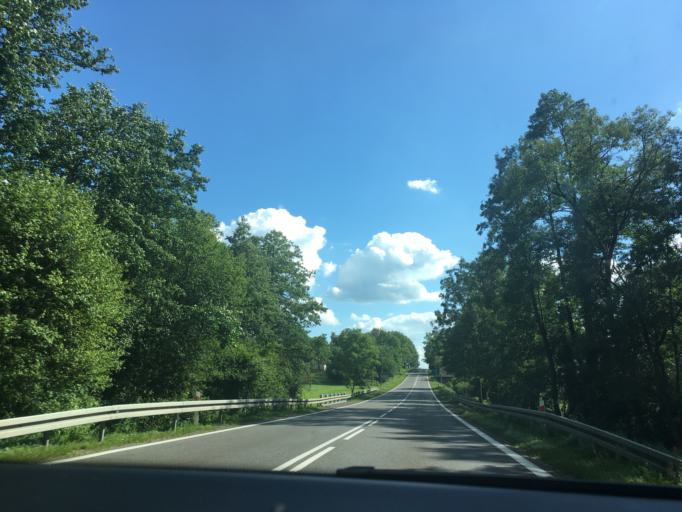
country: PL
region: Podlasie
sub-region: Powiat sokolski
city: Janow
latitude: 53.3955
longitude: 23.1145
